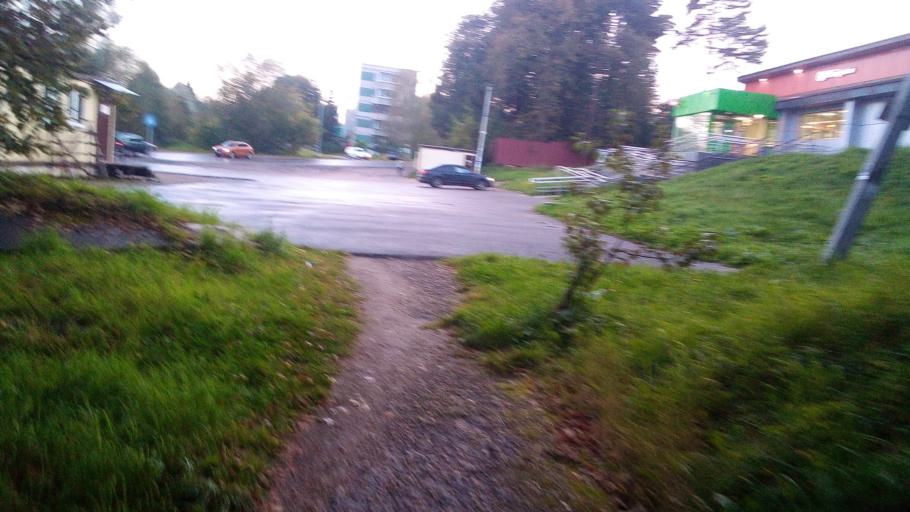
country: RU
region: Moskovskaya
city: Khot'kovo
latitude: 56.2482
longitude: 37.9426
